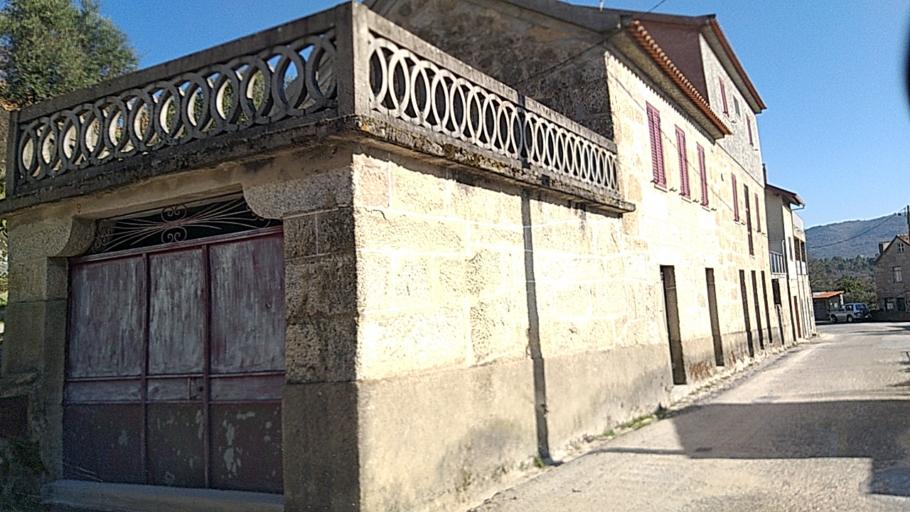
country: PT
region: Guarda
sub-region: Celorico da Beira
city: Celorico da Beira
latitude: 40.6594
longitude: -7.4644
